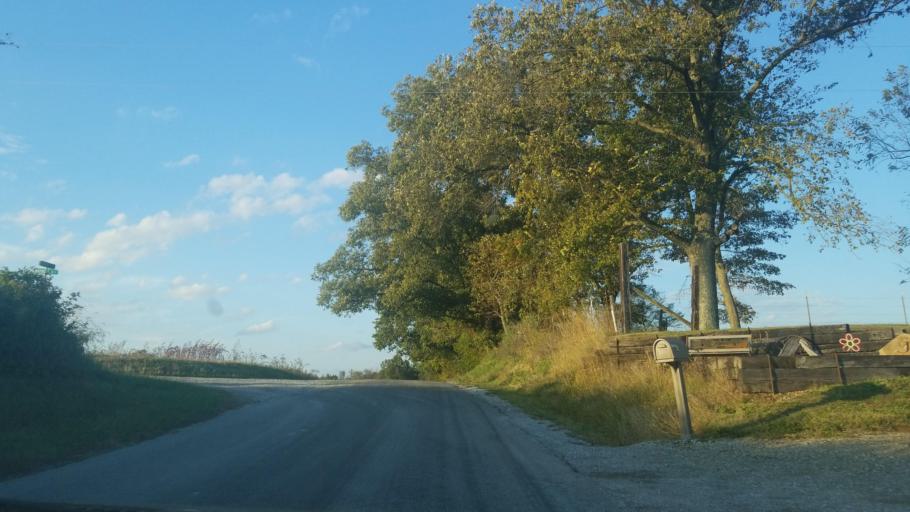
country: US
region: Illinois
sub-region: Saline County
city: Harrisburg
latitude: 37.8120
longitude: -88.6146
